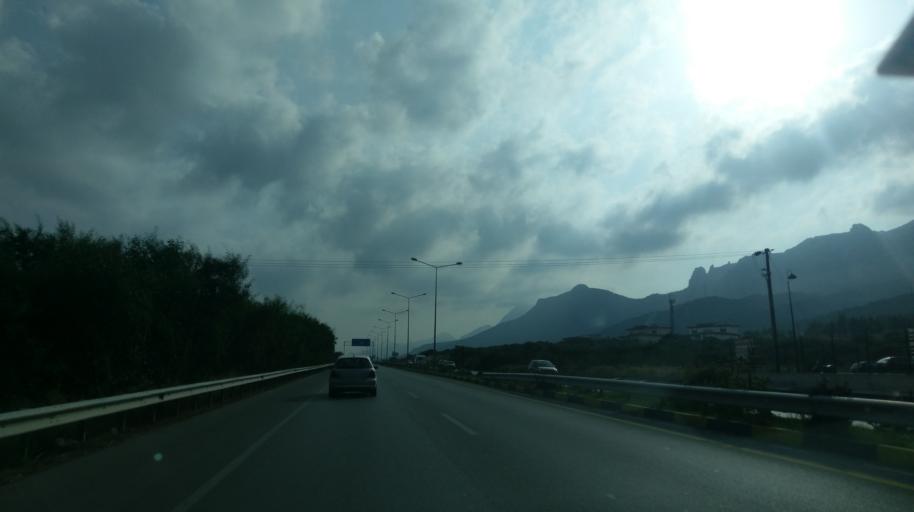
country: CY
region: Keryneia
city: Kyrenia
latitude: 35.3325
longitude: 33.2700
